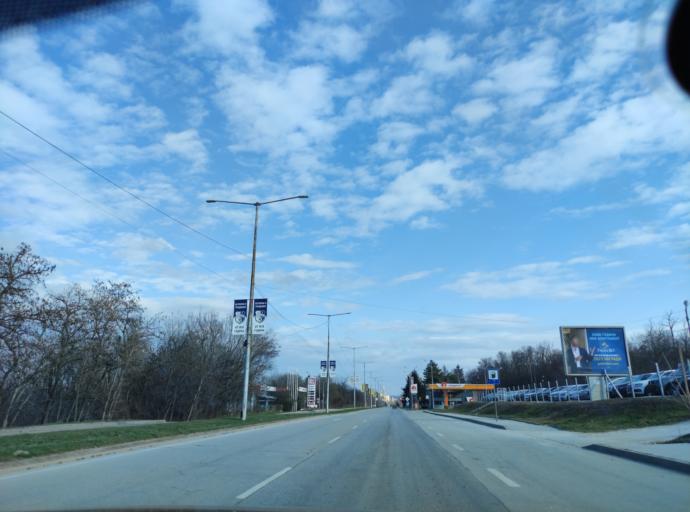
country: BG
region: Pleven
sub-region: Obshtina Pleven
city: Pleven
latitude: 43.4325
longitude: 24.5800
